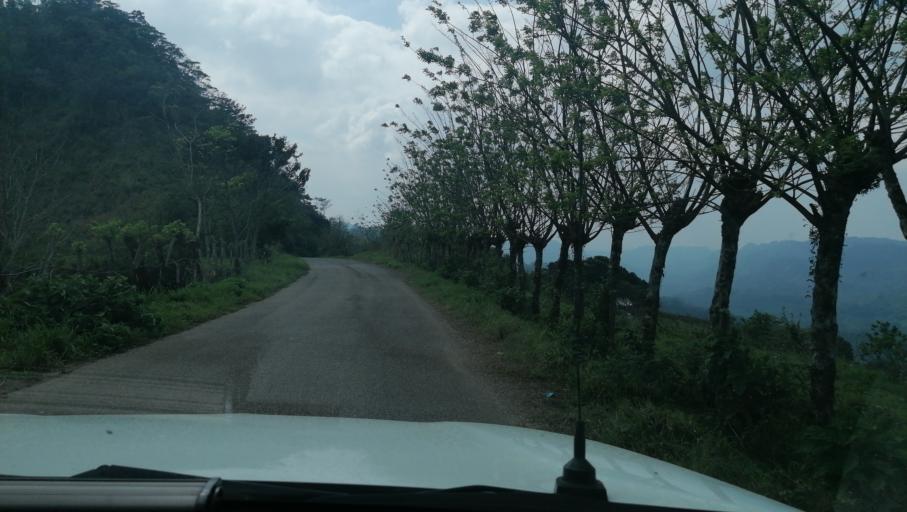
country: MX
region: Chiapas
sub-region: Francisco Leon
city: San Miguel la Sardina
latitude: 17.2375
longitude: -93.3213
